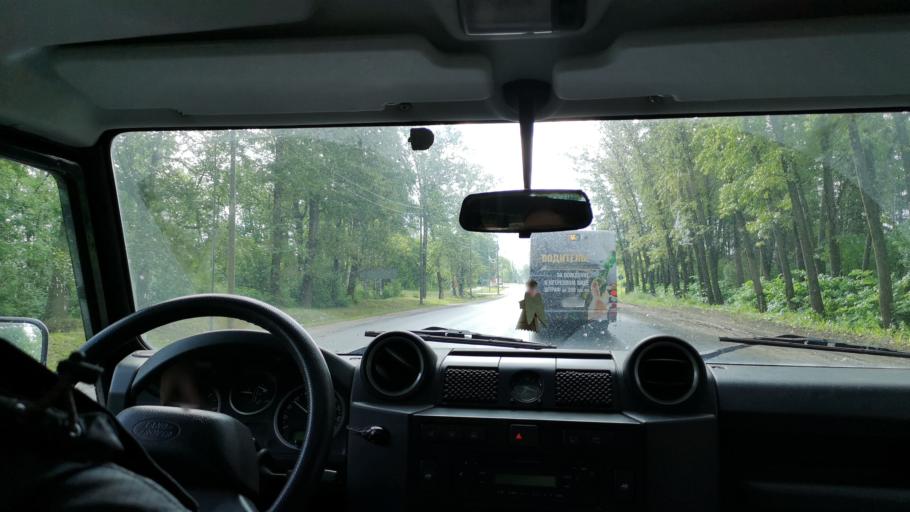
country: RU
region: Moskovskaya
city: Gorshkovo
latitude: 56.3668
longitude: 37.4640
